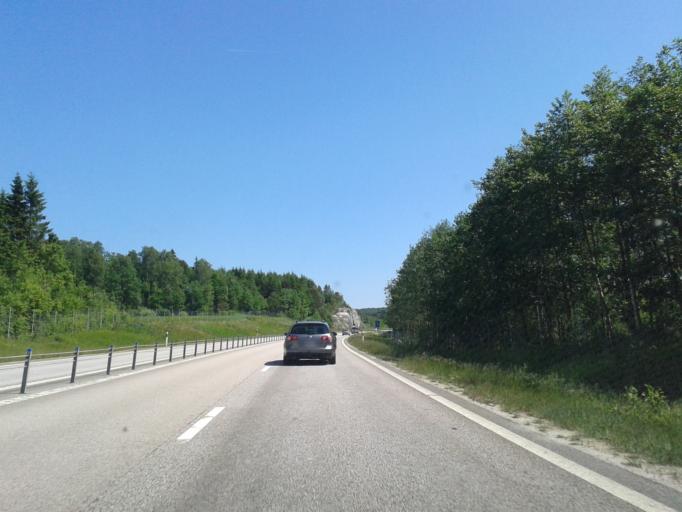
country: SE
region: Vaestra Goetaland
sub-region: Orust
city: Henan
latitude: 58.3493
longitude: 11.7141
